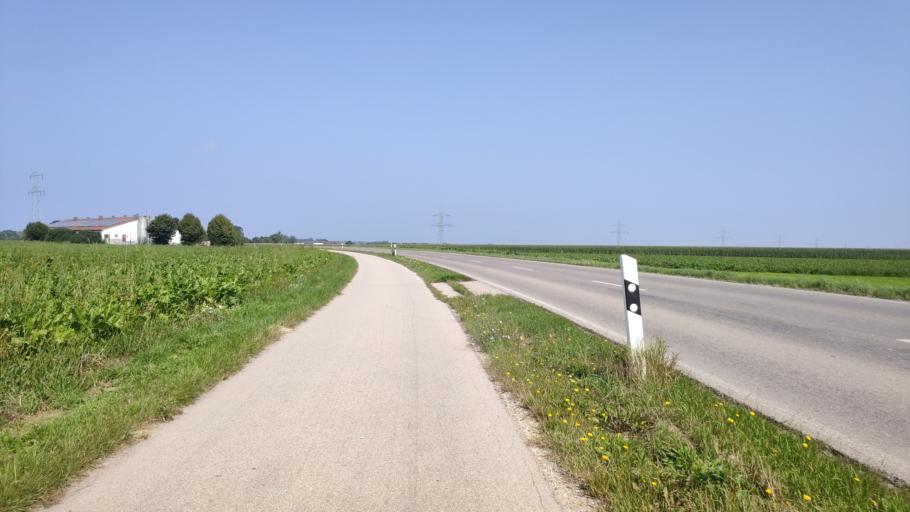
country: DE
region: Bavaria
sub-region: Swabia
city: Oberottmarshausen
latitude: 48.2470
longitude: 10.8498
